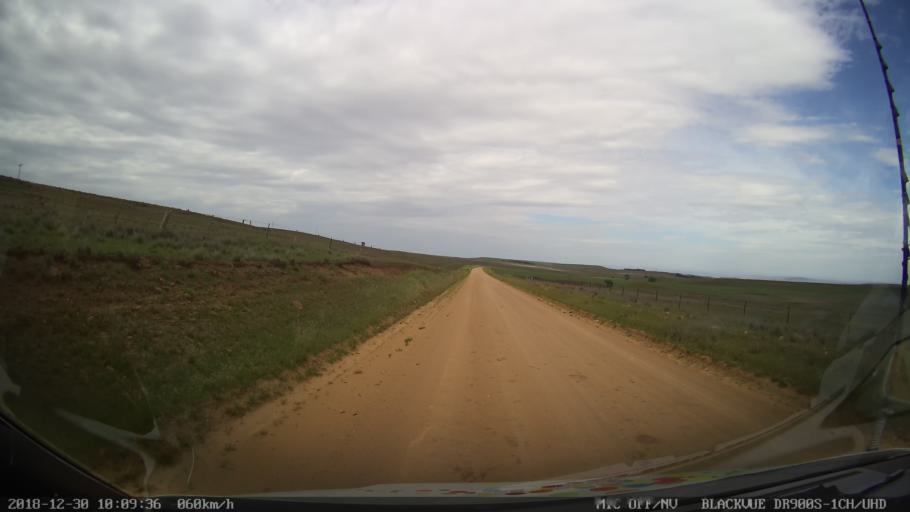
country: AU
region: New South Wales
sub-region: Cooma-Monaro
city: Cooma
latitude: -36.5489
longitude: 149.1038
